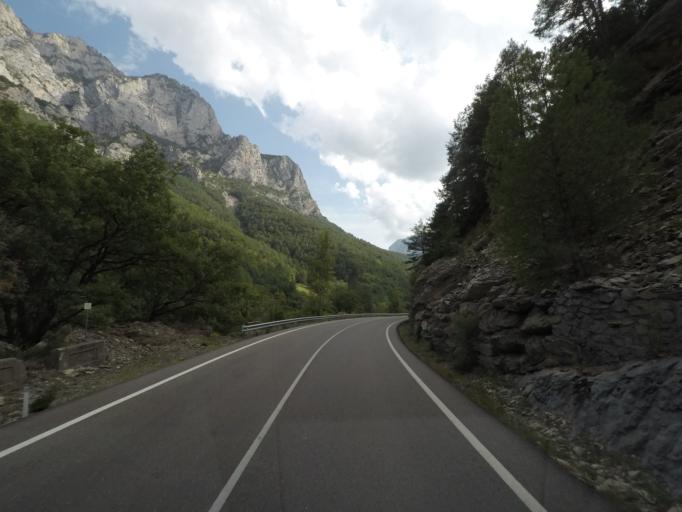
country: ES
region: Aragon
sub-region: Provincia de Huesca
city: Laspuna
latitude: 42.5524
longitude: 0.2024
